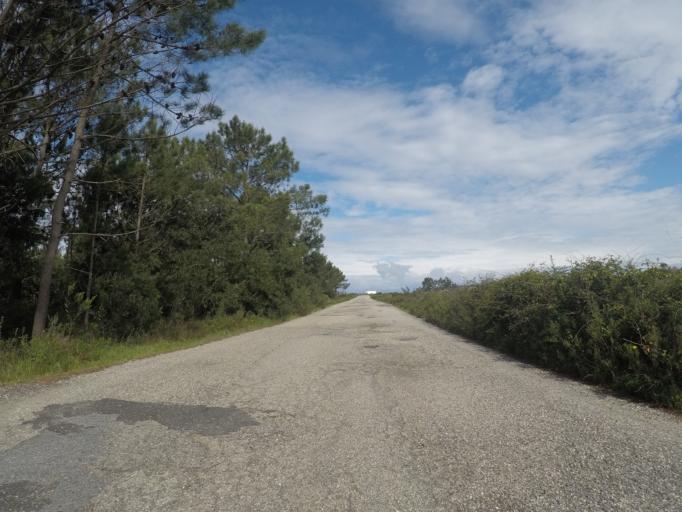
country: PT
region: Beja
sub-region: Odemira
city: Sao Teotonio
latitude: 37.4479
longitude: -8.7636
